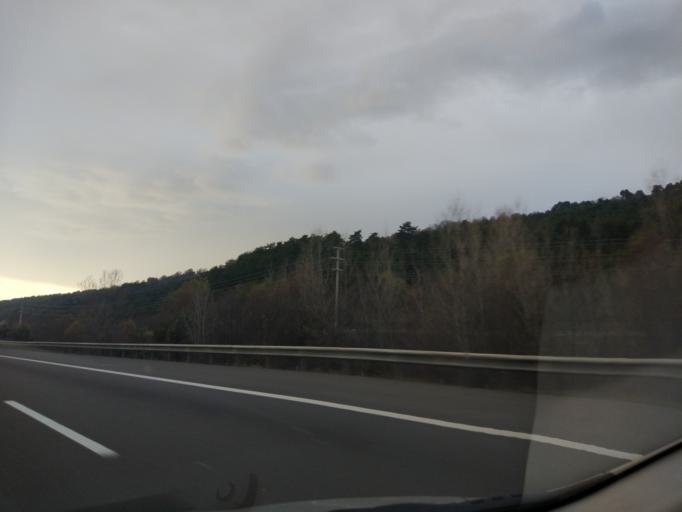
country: TR
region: Bolu
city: Yenicaga
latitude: 40.7423
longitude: 31.8497
